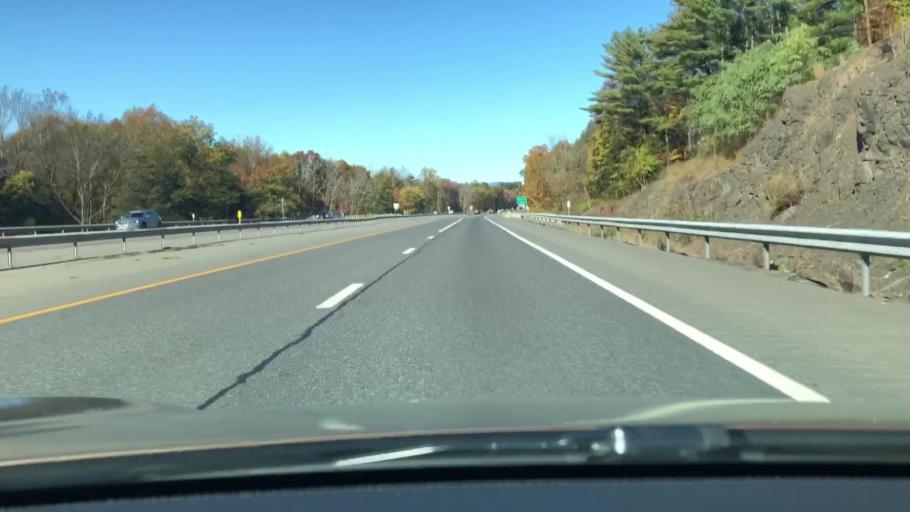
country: US
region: New York
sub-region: Ulster County
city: Tillson
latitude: 41.8157
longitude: -74.0556
